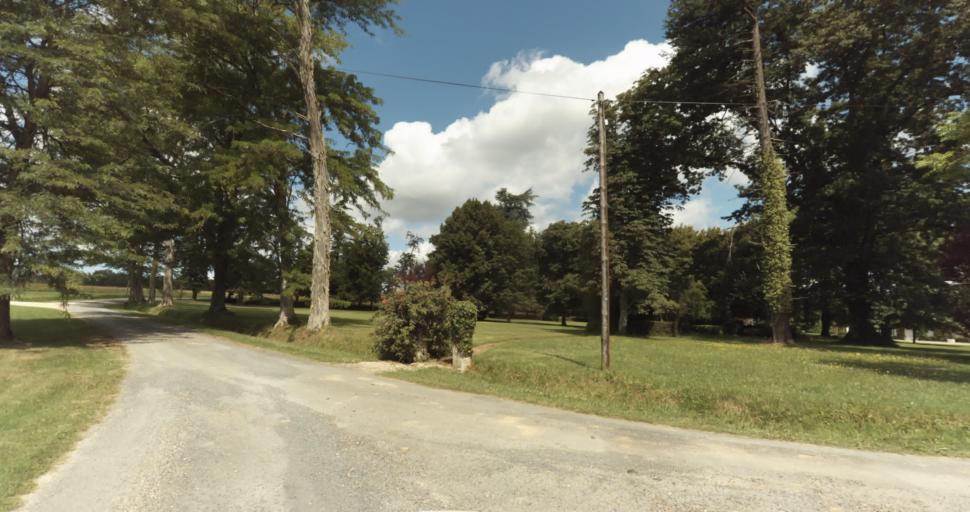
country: FR
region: Aquitaine
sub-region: Departement de la Gironde
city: Bazas
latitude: 44.4581
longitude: -0.1735
